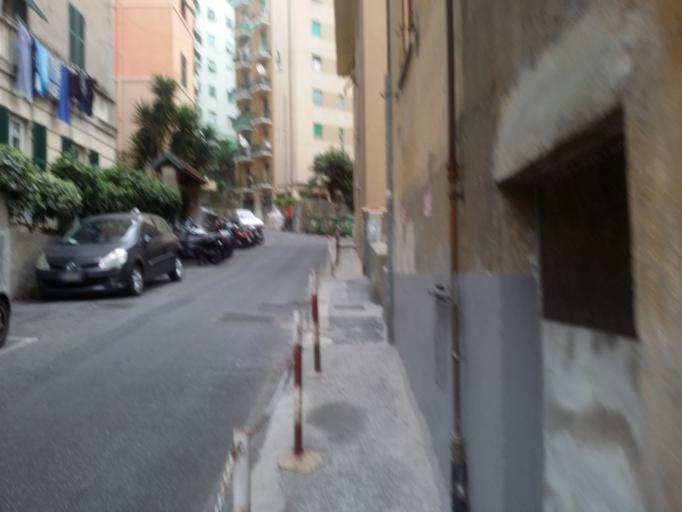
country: IT
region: Liguria
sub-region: Provincia di Genova
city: Genoa
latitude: 44.4092
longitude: 8.9624
